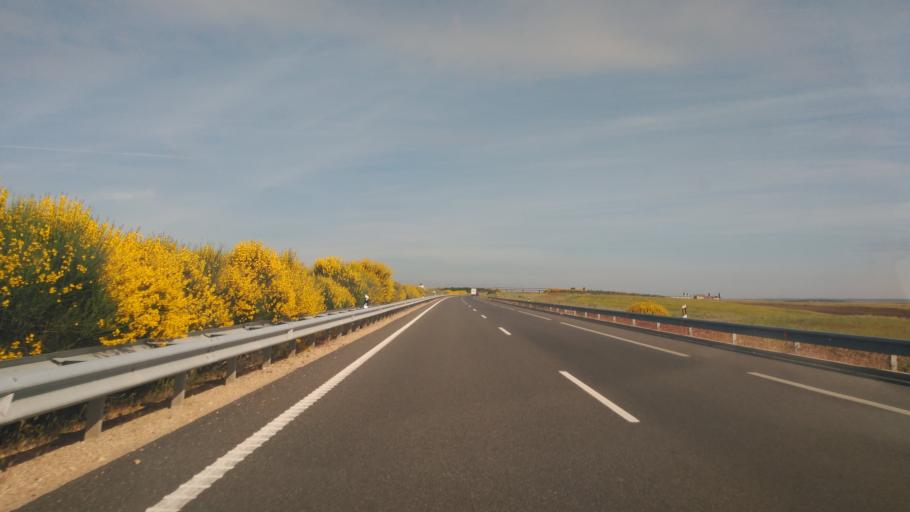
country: ES
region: Castille and Leon
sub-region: Provincia de Salamanca
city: Castellanos de Villiquera
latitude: 41.0547
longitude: -5.6749
